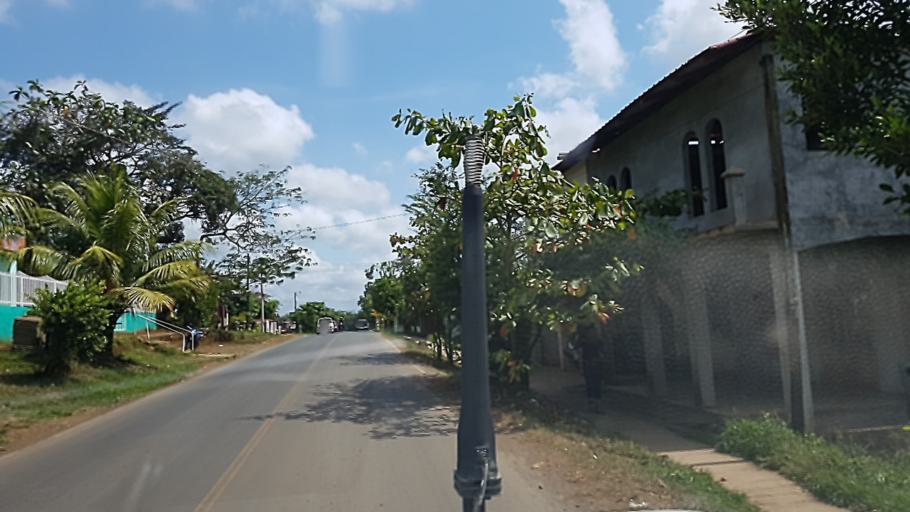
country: NI
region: Atlantico Sur
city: Nueva Guinea
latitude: 11.6923
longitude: -84.4621
